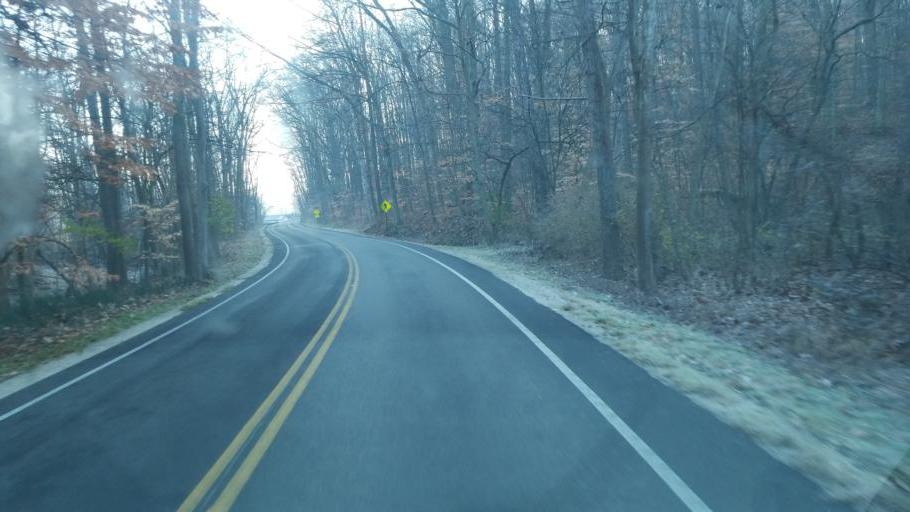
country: US
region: Ohio
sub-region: Summit County
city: Fairlawn
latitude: 41.1365
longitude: -81.5668
